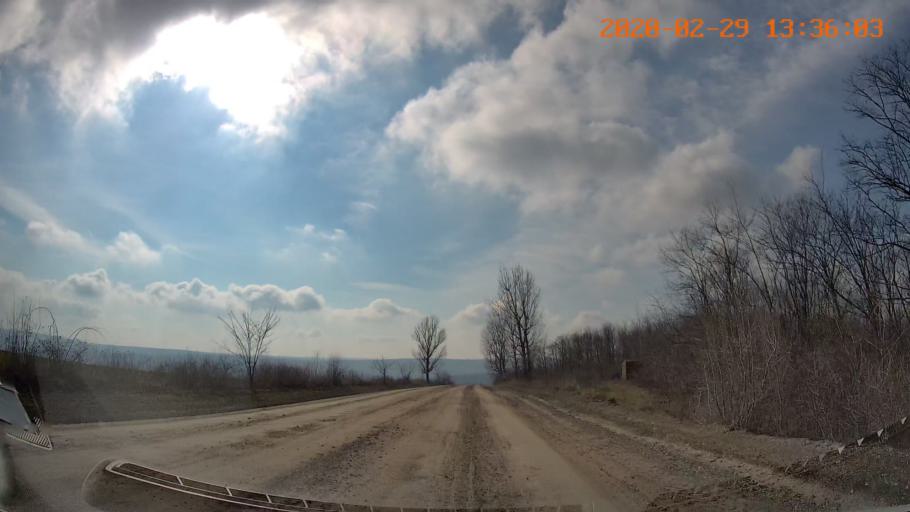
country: MD
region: Telenesti
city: Camenca
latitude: 47.8631
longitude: 28.6087
